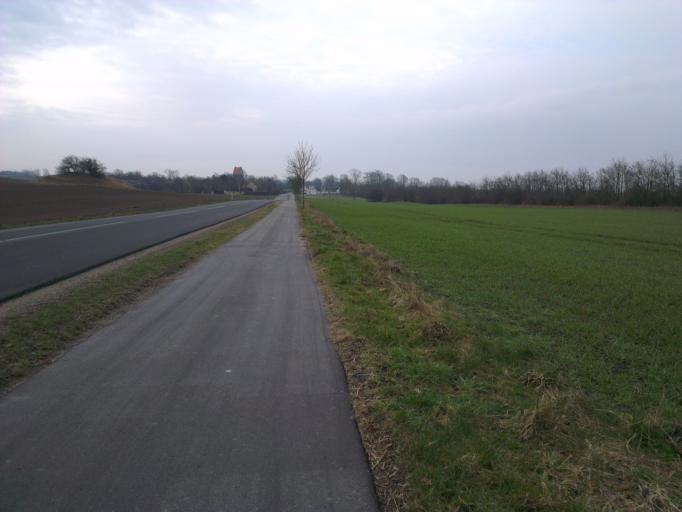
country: DK
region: Capital Region
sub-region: Frederikssund Kommune
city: Skibby
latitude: 55.7662
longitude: 11.9089
